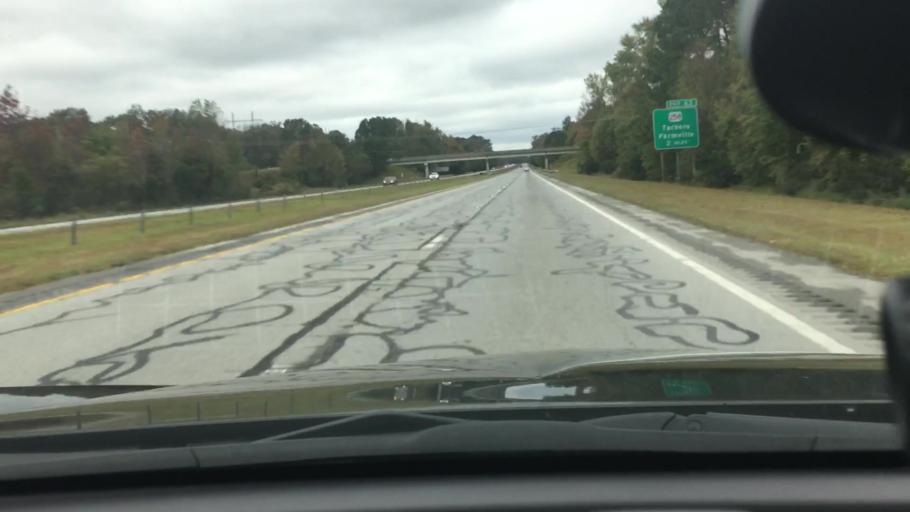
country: US
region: North Carolina
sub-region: Pitt County
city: Farmville
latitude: 35.6072
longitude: -77.5713
